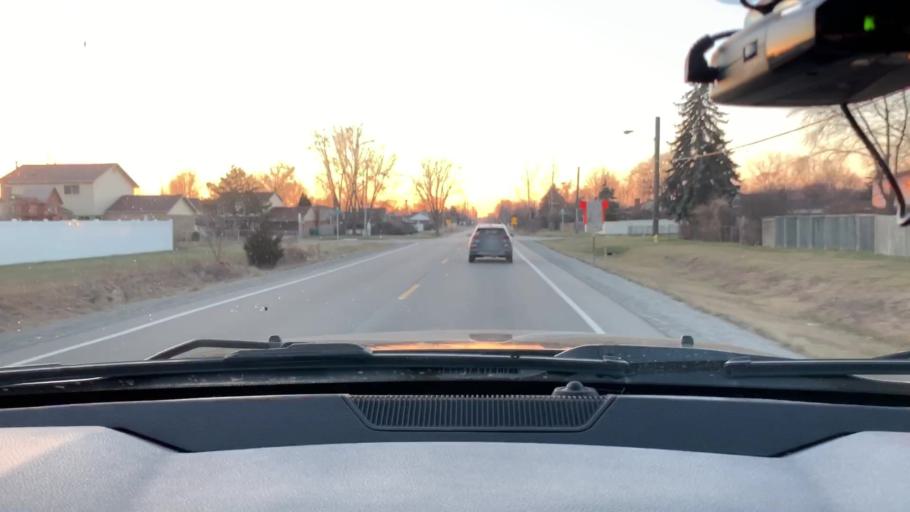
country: US
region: Michigan
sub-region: Wayne County
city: Flat Rock
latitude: 42.1236
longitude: -83.2856
